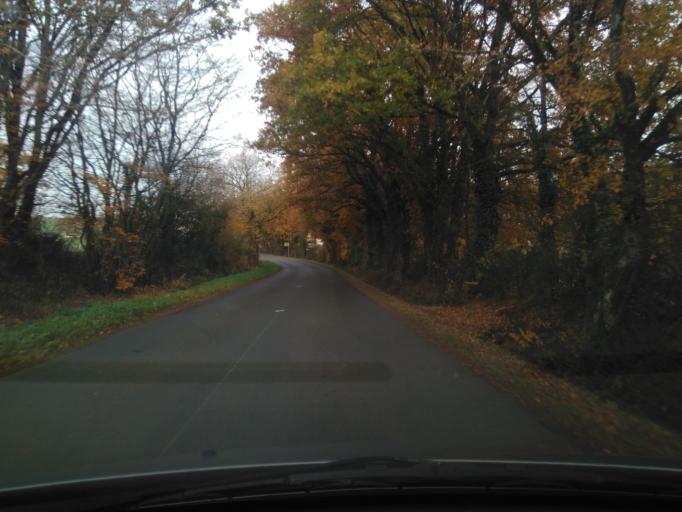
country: FR
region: Pays de la Loire
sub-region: Departement de la Vendee
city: Saint-Florent-des-Bois
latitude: 46.5875
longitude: -1.3163
